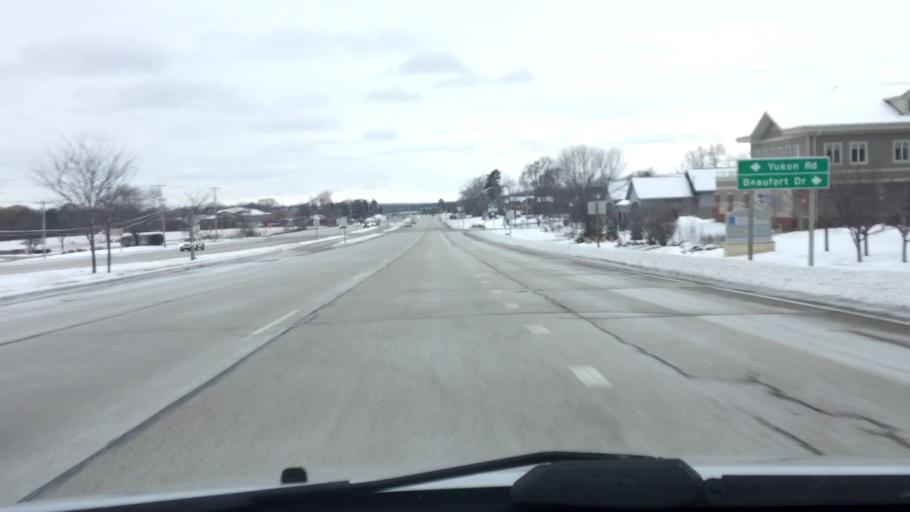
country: US
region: Wisconsin
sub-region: Waukesha County
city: Brookfield
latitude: 43.0903
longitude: -88.1285
